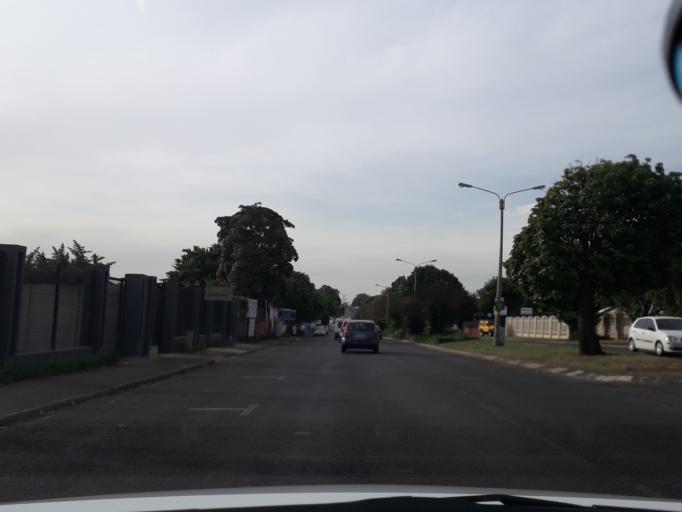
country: ZA
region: Gauteng
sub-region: City of Johannesburg Metropolitan Municipality
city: Modderfontein
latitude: -26.1531
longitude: 28.1523
